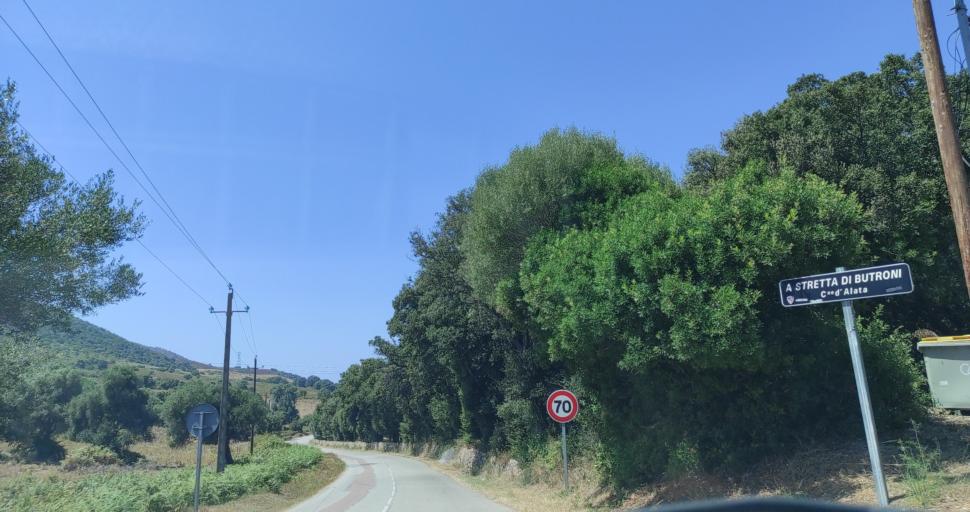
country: FR
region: Corsica
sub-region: Departement de la Corse-du-Sud
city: Alata
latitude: 41.9631
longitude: 8.7241
